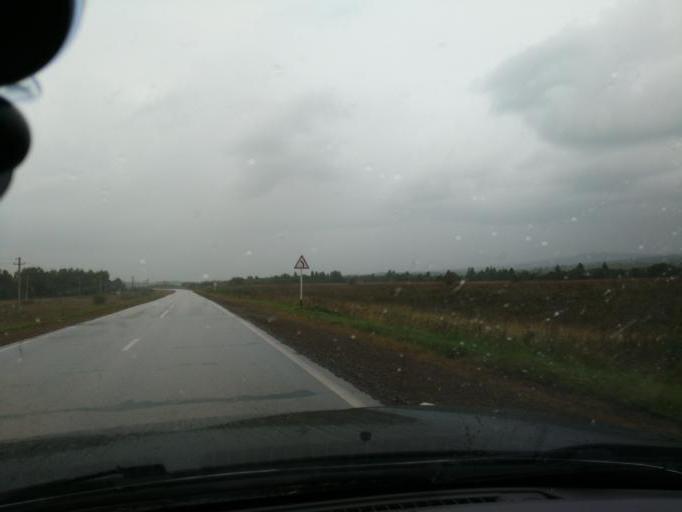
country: RU
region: Perm
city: Barda
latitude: 57.0774
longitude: 55.5426
